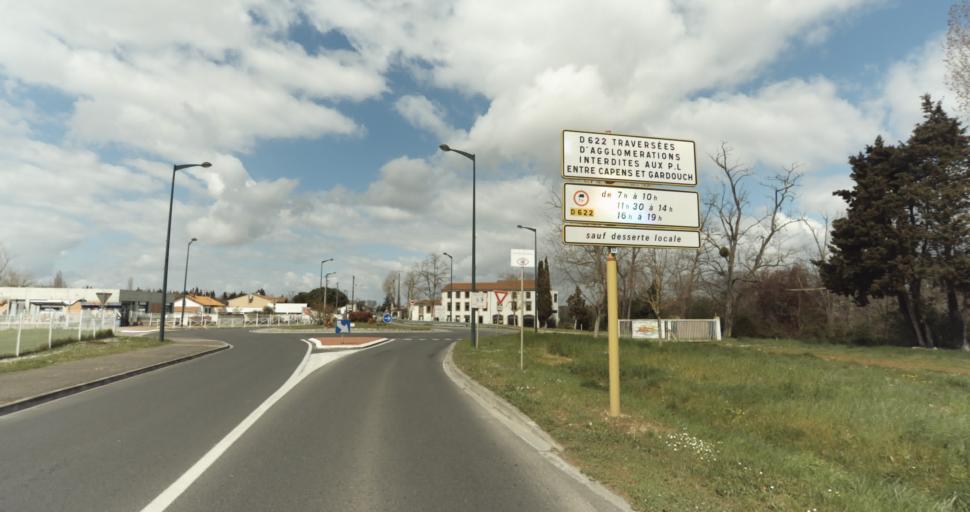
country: FR
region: Midi-Pyrenees
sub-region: Departement de la Haute-Garonne
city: Auterive
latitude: 43.3431
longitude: 1.4761
